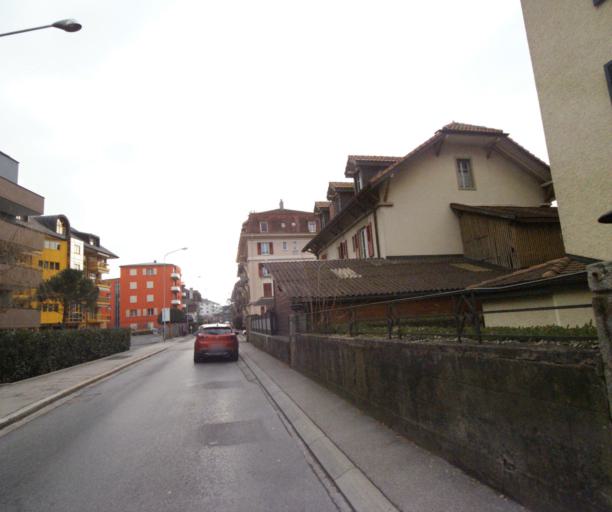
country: CH
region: Vaud
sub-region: Riviera-Pays-d'Enhaut District
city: La Tour-de-Peilz
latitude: 46.4555
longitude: 6.8576
